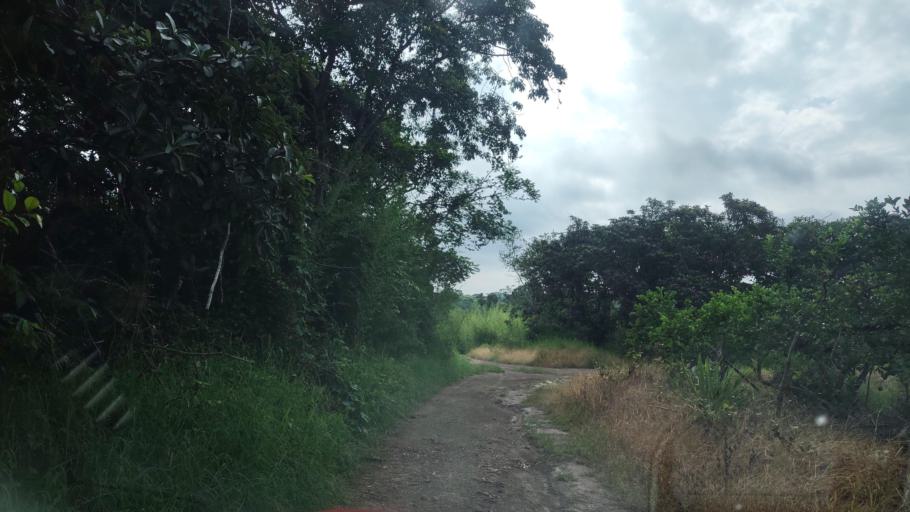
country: MX
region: Veracruz
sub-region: Coatepec
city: Bella Esperanza
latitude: 19.4468
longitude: -96.8276
